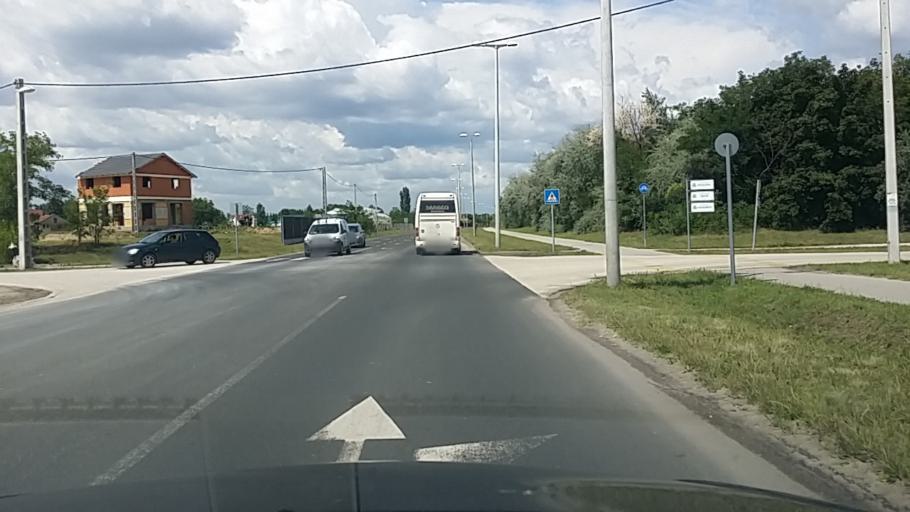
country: HU
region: Bacs-Kiskun
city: Kecskemet
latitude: 46.8908
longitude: 19.6399
